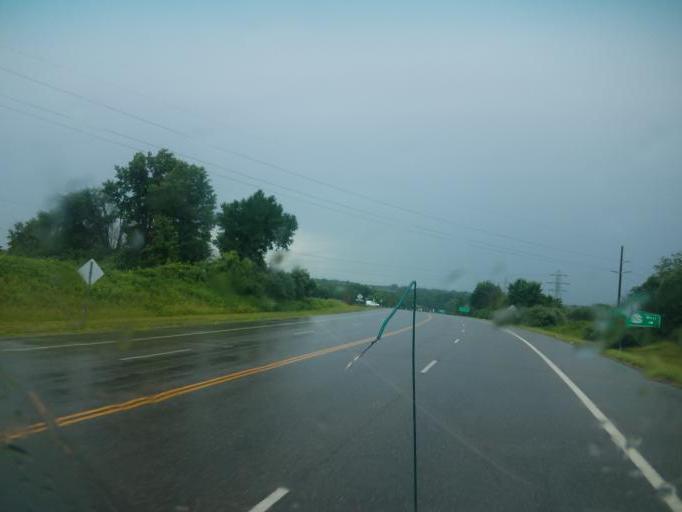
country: US
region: Ohio
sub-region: Stark County
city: Massillon
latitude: 40.7702
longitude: -81.5784
